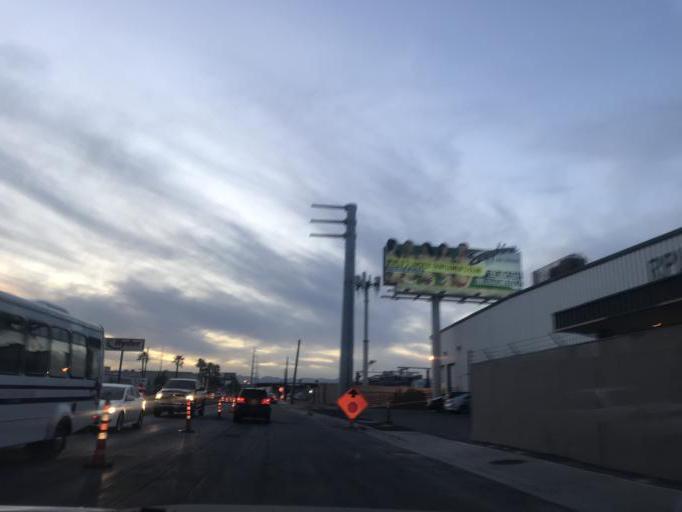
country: US
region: Nevada
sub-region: Clark County
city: Paradise
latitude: 36.1083
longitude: -115.1835
